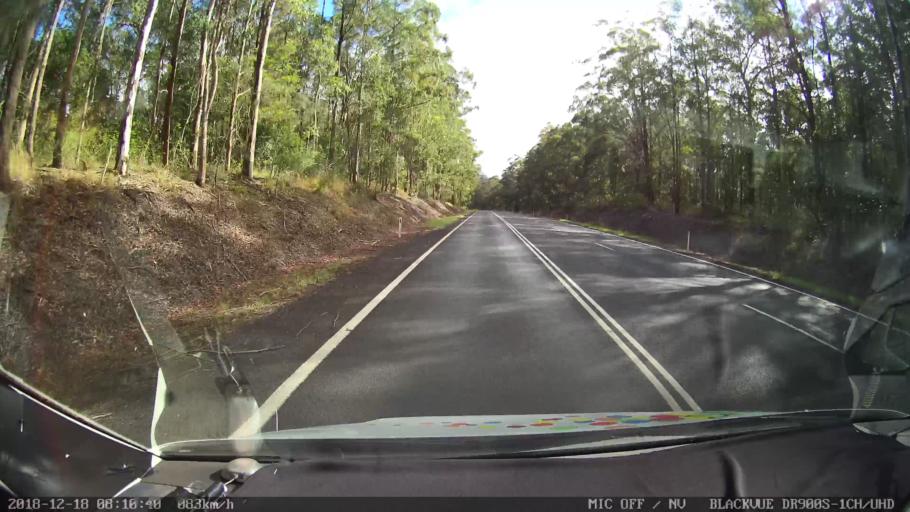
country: AU
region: New South Wales
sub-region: Kyogle
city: Kyogle
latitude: -28.3591
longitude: 152.6636
